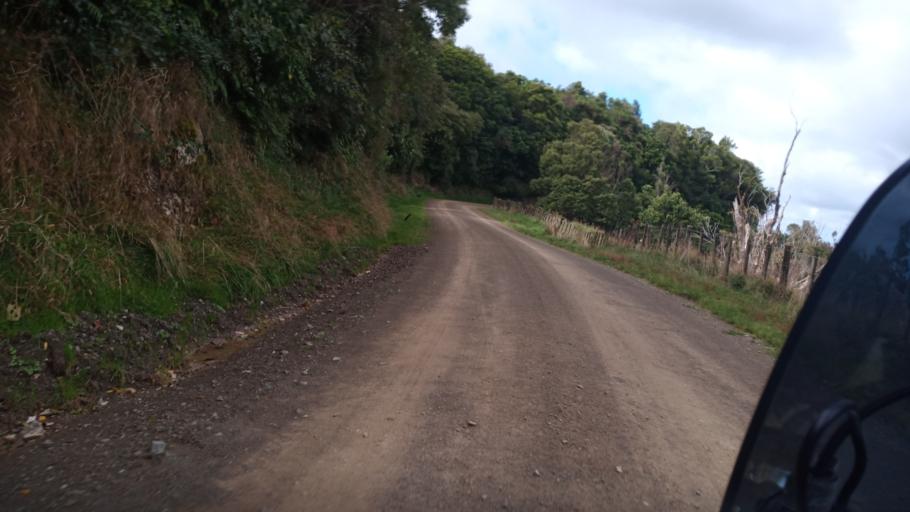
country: NZ
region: Gisborne
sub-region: Gisborne District
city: Gisborne
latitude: -38.4841
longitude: 177.5986
